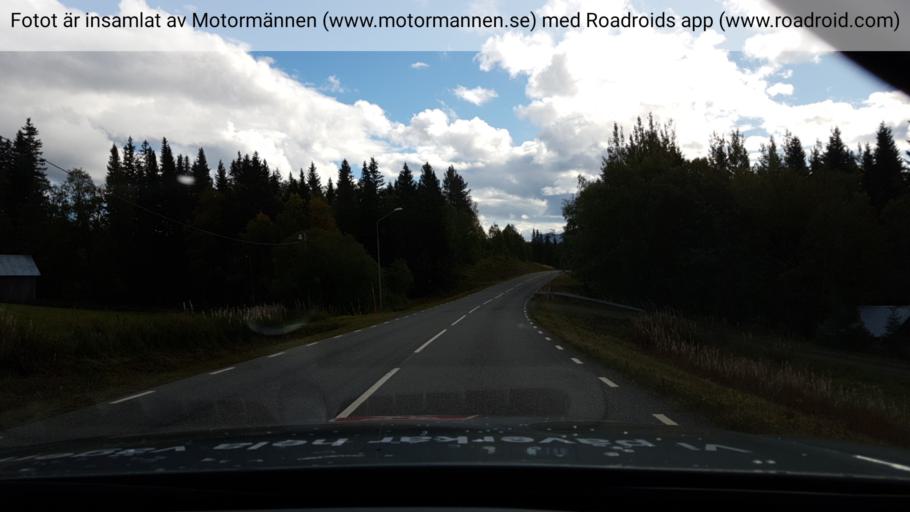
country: SE
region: Jaemtland
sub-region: Are Kommun
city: Are
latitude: 63.5671
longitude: 13.0242
